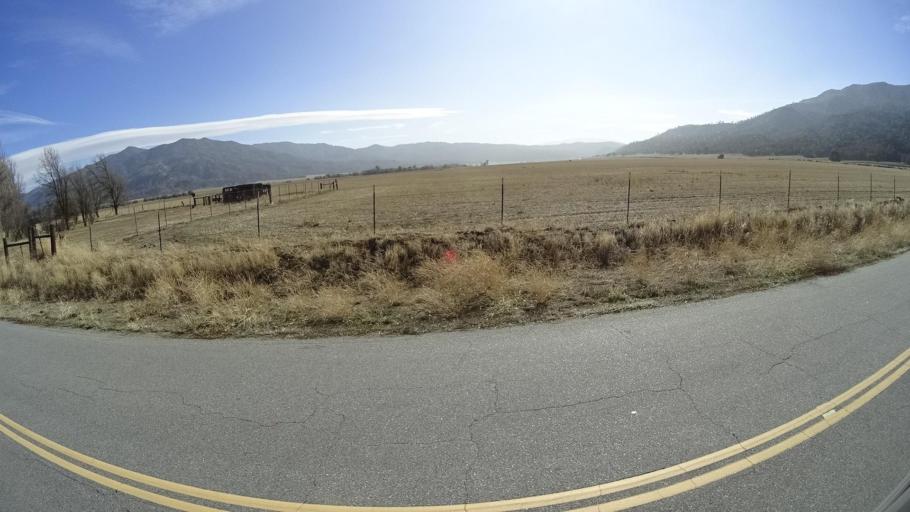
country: US
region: California
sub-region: Kern County
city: Bodfish
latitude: 35.4194
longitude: -118.5401
